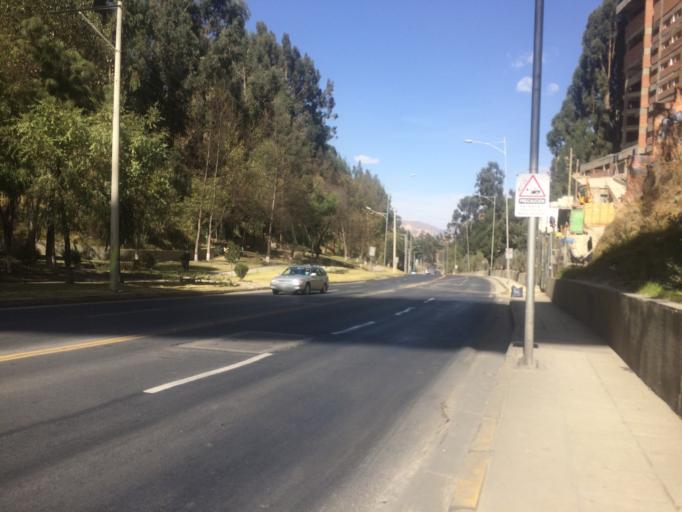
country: BO
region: La Paz
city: La Paz
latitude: -16.5082
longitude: -68.1229
